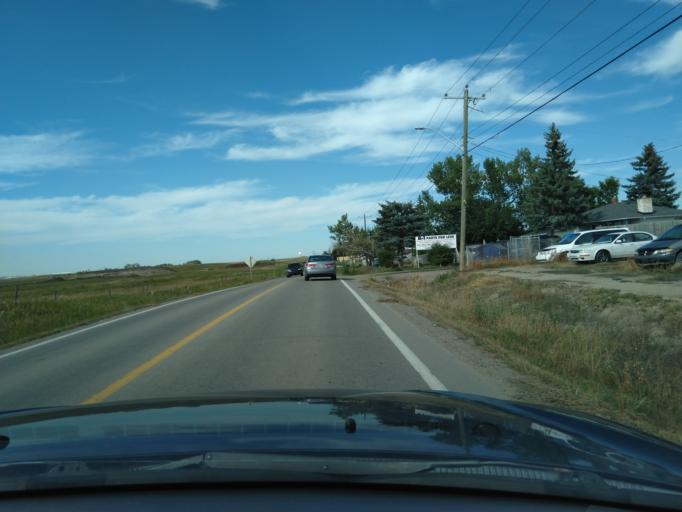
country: CA
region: Alberta
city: Calgary
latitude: 51.1180
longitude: -113.9817
